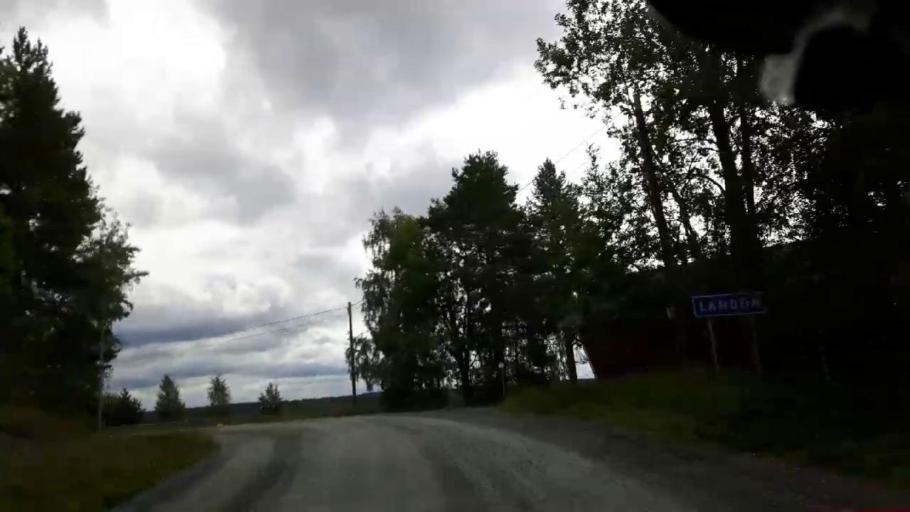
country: SE
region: Jaemtland
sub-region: Krokoms Kommun
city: Krokom
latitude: 63.5693
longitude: 14.2402
